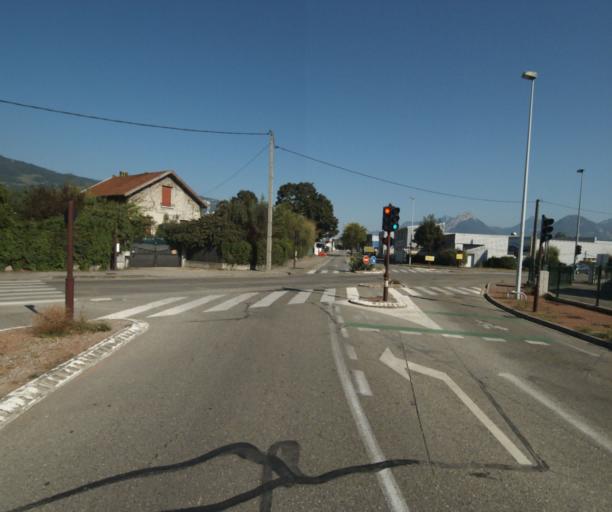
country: FR
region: Rhone-Alpes
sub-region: Departement de l'Isere
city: Le Pont-de-Claix
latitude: 45.1425
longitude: 5.7088
